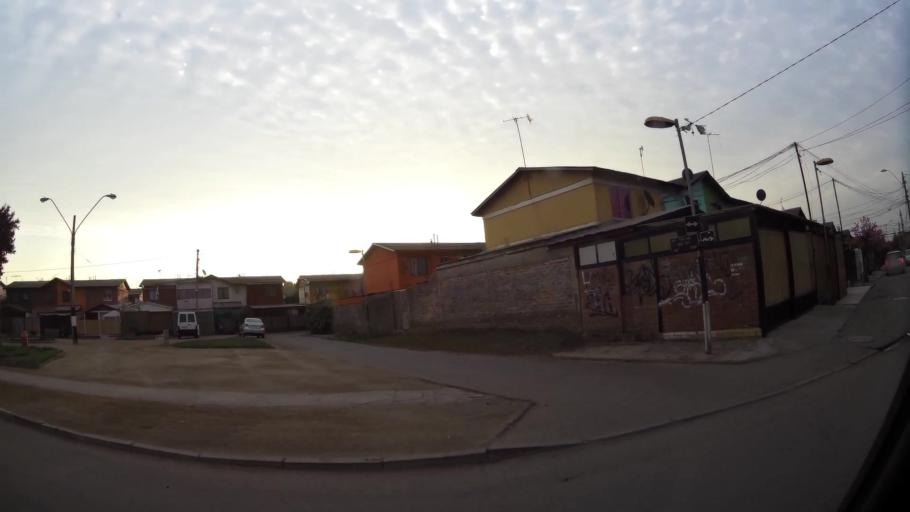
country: CL
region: Santiago Metropolitan
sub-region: Provincia de Santiago
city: Lo Prado
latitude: -33.5075
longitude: -70.7921
